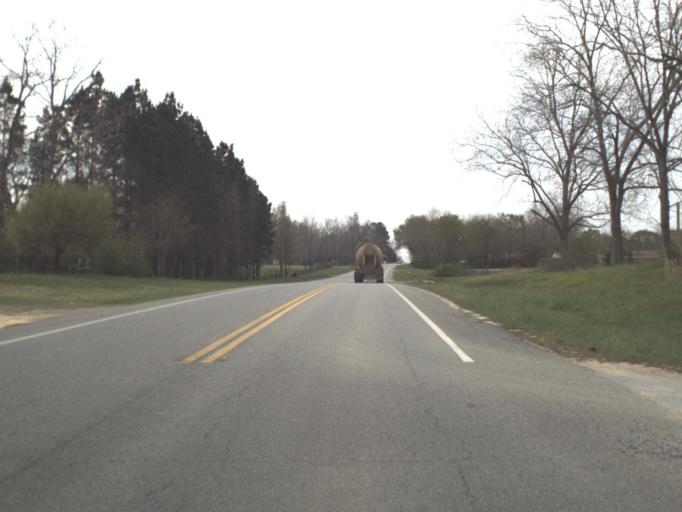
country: US
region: Florida
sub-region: Holmes County
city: Bonifay
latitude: 30.9149
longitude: -85.6496
